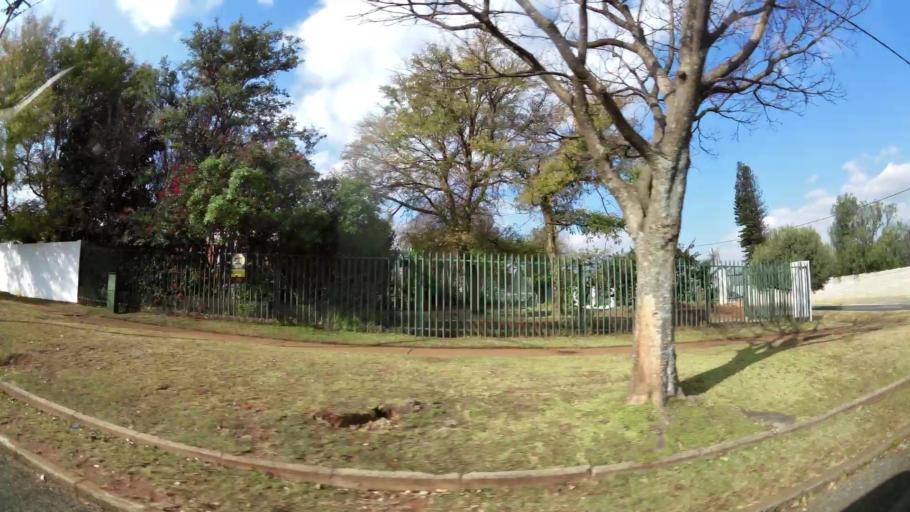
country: ZA
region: Gauteng
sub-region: West Rand District Municipality
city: Krugersdorp
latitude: -26.0864
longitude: 27.7679
